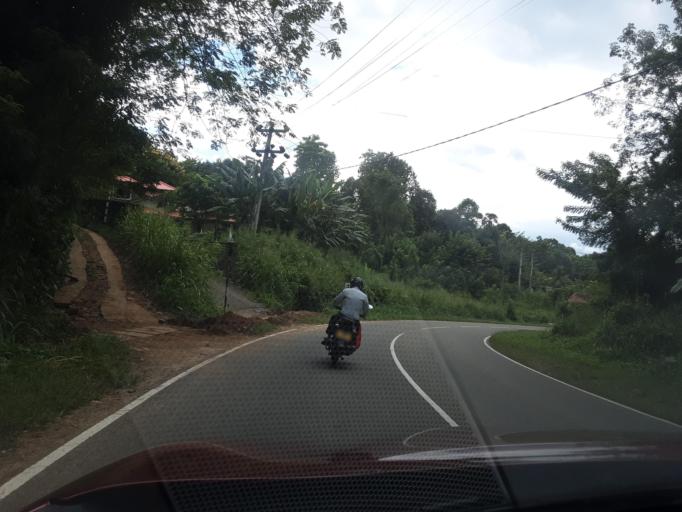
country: LK
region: Uva
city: Monaragala
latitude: 6.9078
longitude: 81.2221
